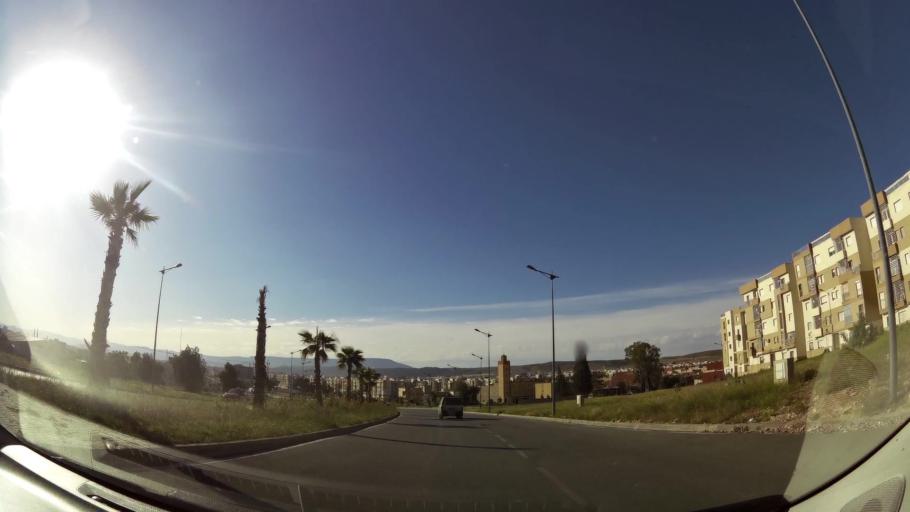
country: MA
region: Oriental
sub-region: Oujda-Angad
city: Oujda
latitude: 34.6662
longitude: -1.9205
